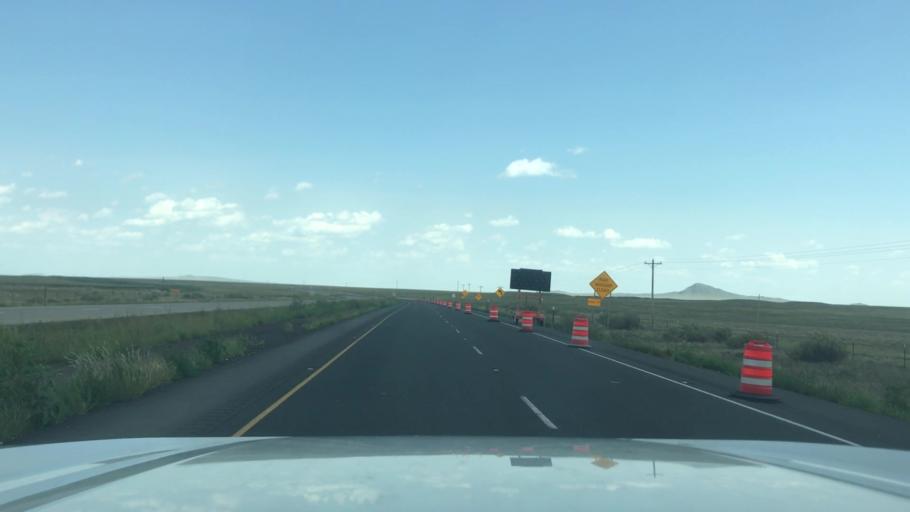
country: US
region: New Mexico
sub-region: Union County
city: Clayton
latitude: 36.6172
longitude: -103.6898
